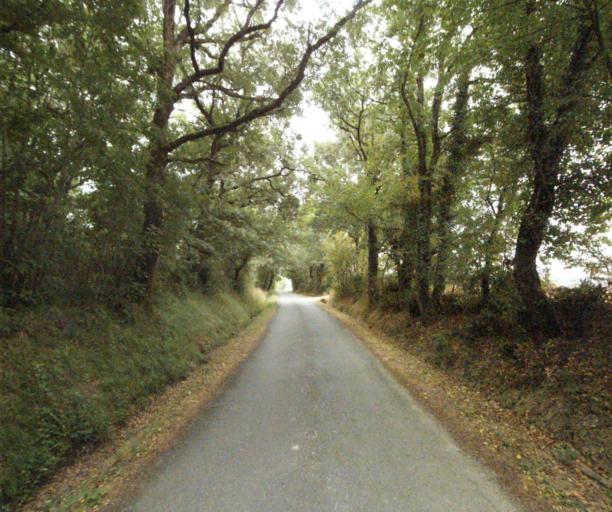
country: FR
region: Midi-Pyrenees
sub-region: Departement du Tarn
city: Soreze
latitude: 43.4745
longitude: 2.0655
